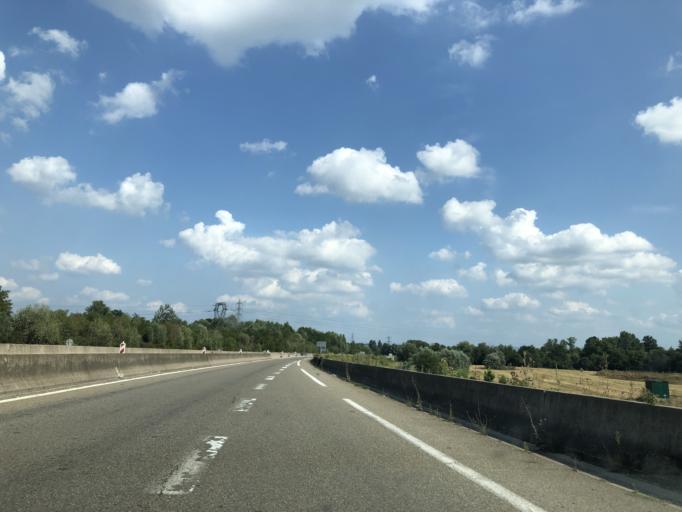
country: FR
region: Alsace
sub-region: Departement du Bas-Rhin
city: Eschau
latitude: 48.5076
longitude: 7.7011
